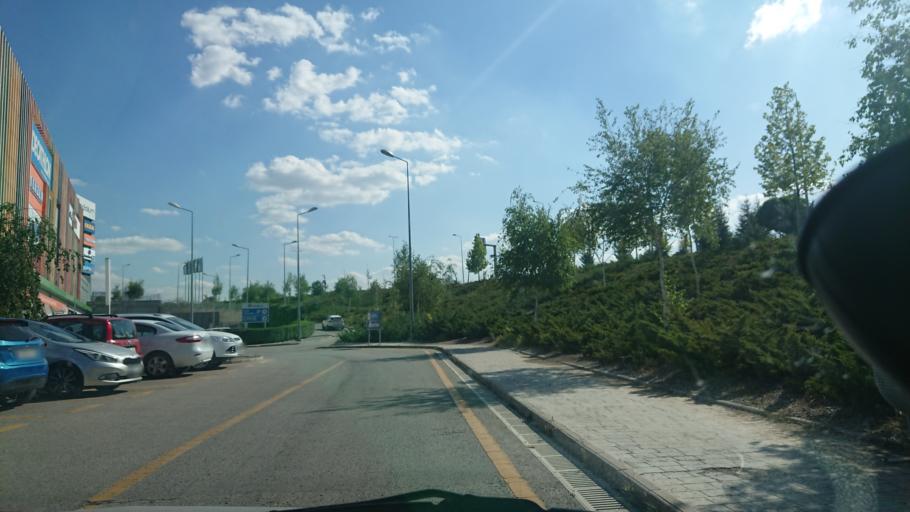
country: TR
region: Ankara
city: Mamak
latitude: 39.8879
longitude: 32.9314
